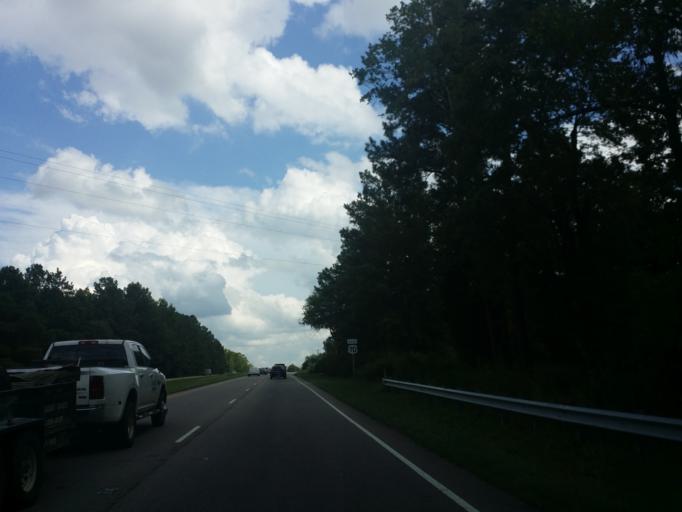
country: US
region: North Carolina
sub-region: Wake County
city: Morrisville
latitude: 35.9227
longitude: -78.7964
